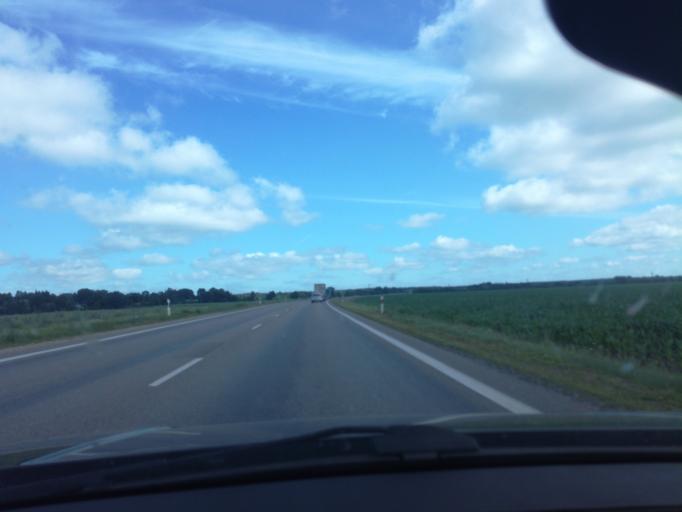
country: LT
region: Panevezys
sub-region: Panevezys City
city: Panevezys
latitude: 55.7909
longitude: 24.3133
